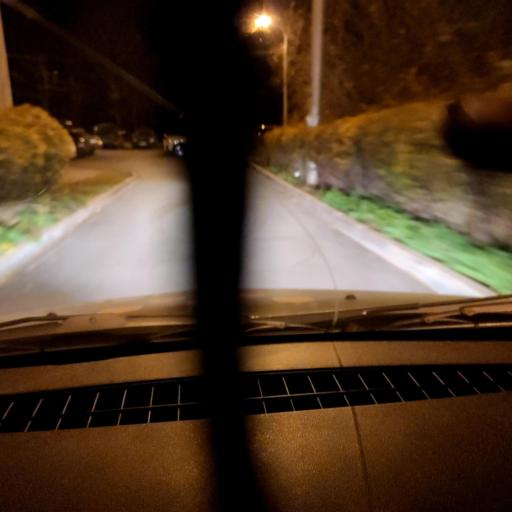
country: RU
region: Bashkortostan
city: Ufa
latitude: 54.7595
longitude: 55.9919
